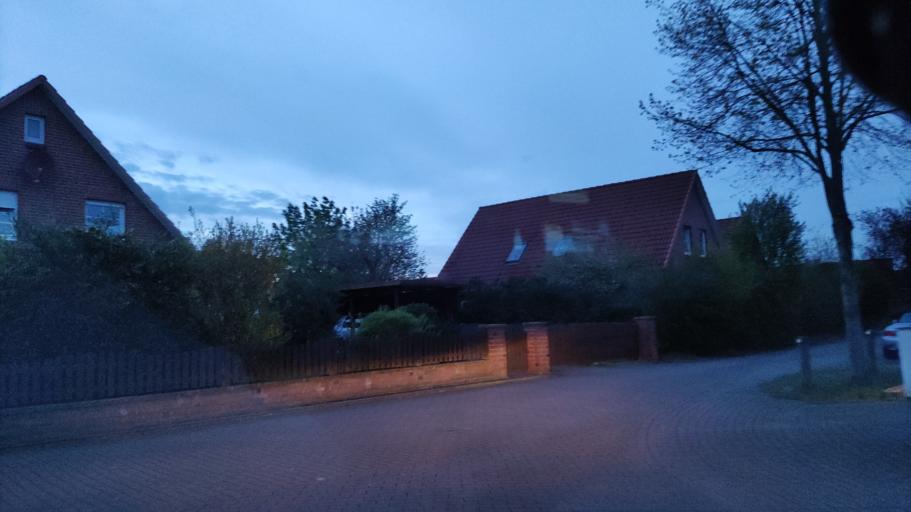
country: DE
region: Lower Saxony
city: Bardowick
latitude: 53.2886
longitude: 10.3828
